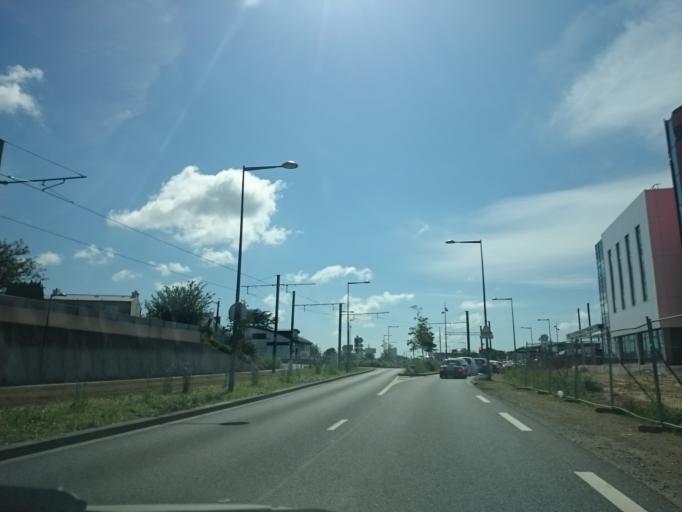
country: FR
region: Brittany
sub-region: Departement du Finistere
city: Gouesnou
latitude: 48.4191
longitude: -4.4512
